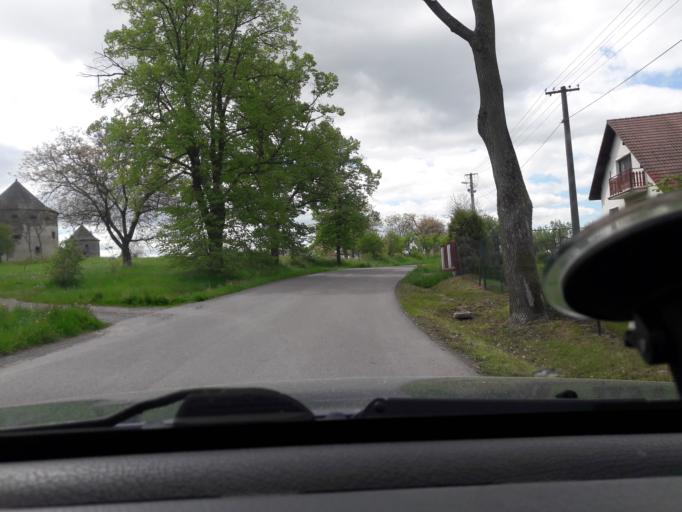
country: SK
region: Banskobystricky
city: Krupina
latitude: 48.3169
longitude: 19.0894
